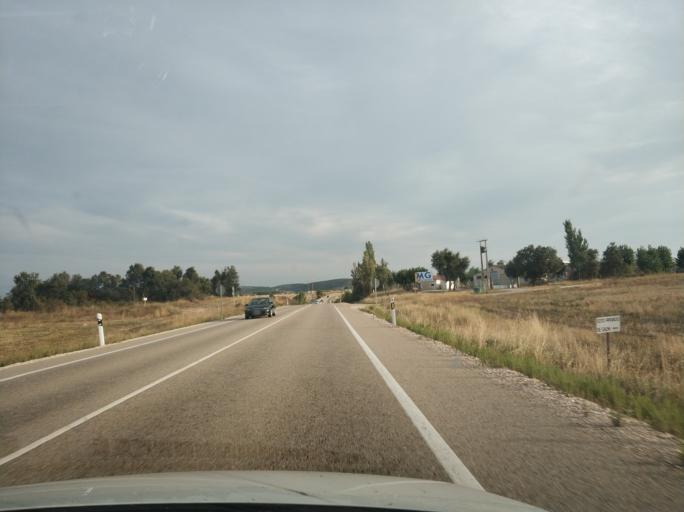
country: ES
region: Castille and Leon
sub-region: Provincia de Burgos
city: Revillarruz
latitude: 42.2109
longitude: -3.6511
